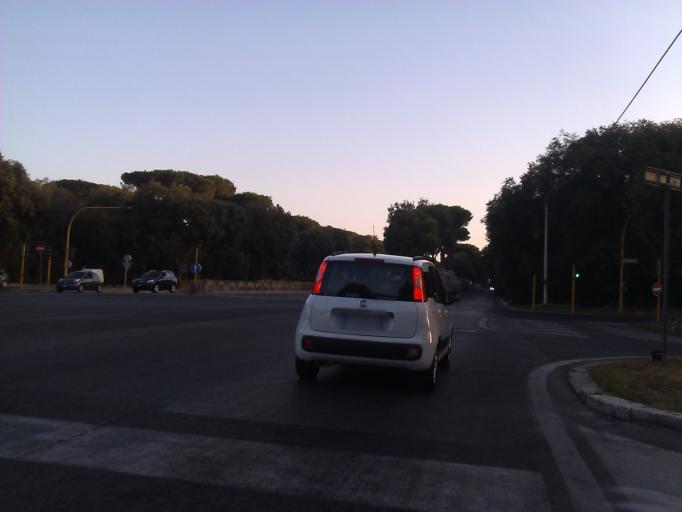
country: IT
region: Latium
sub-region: Citta metropolitana di Roma Capitale
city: Acilia-Castel Fusano-Ostia Antica
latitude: 41.7231
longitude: 12.3281
